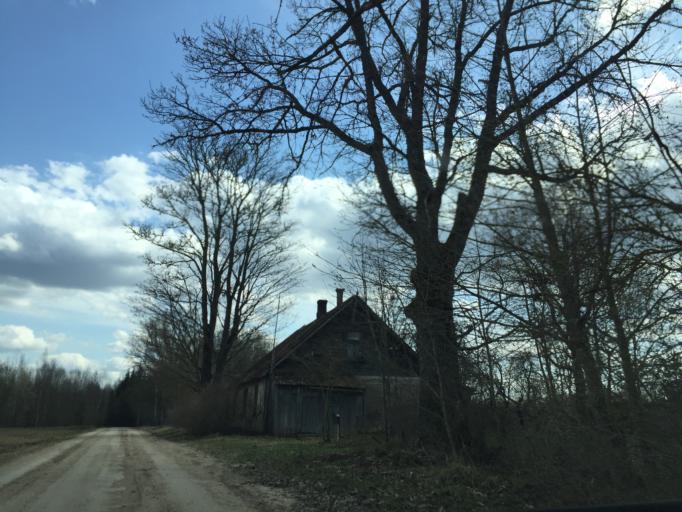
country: LV
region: Skriveri
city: Skriveri
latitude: 56.7581
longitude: 25.1595
